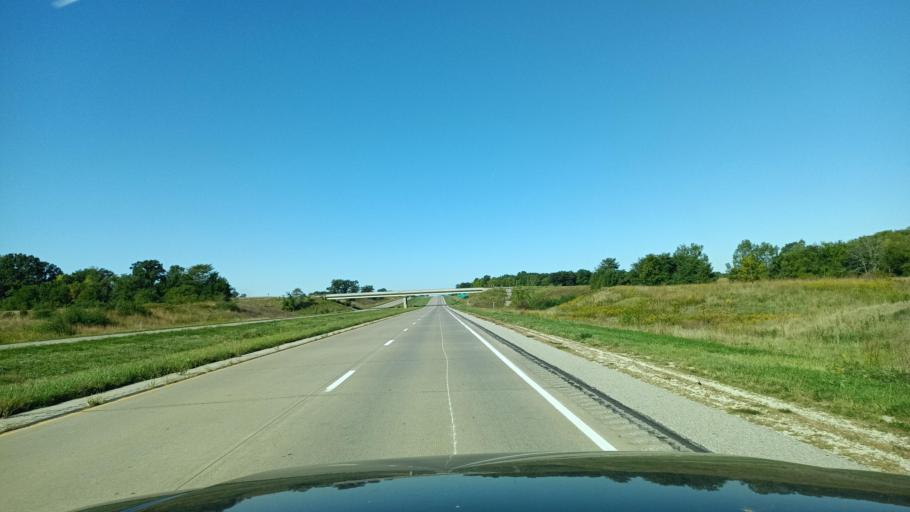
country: US
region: Iowa
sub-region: Lee County
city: Fort Madison
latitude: 40.6707
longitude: -91.2976
